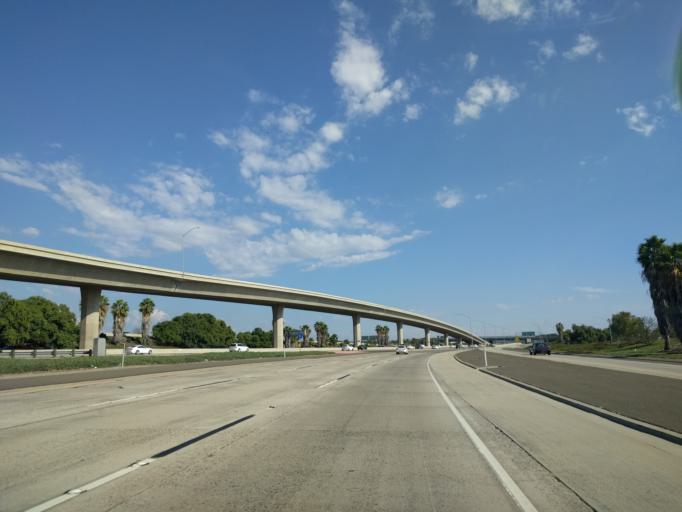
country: US
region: California
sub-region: Orange County
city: Laguna Woods
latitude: 33.6437
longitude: -117.7352
